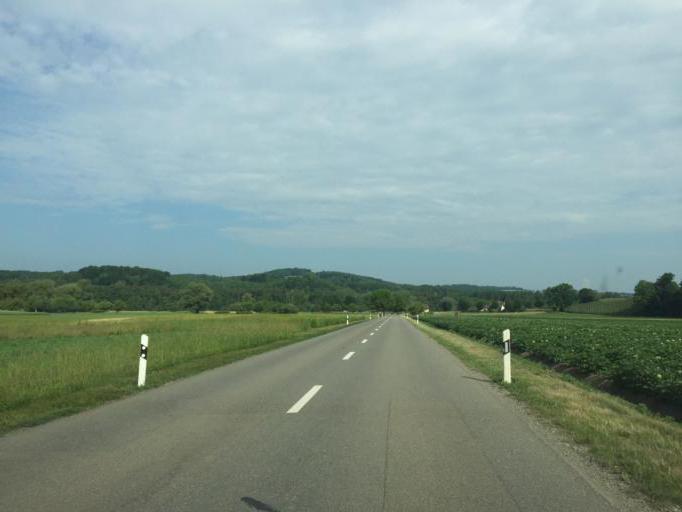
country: DE
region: Baden-Wuerttemberg
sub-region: Freiburg Region
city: Lottstetten
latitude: 47.6002
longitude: 8.6048
